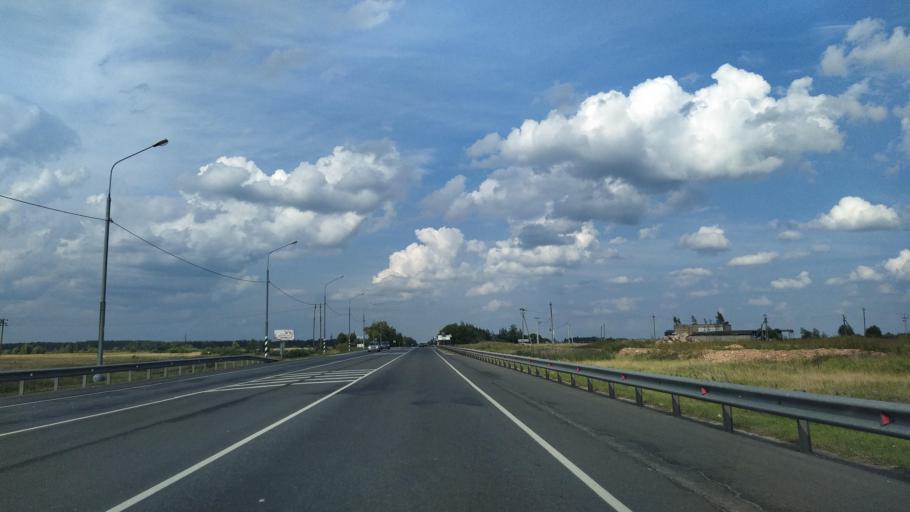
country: RU
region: Novgorod
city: Shimsk
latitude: 58.2216
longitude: 30.7411
